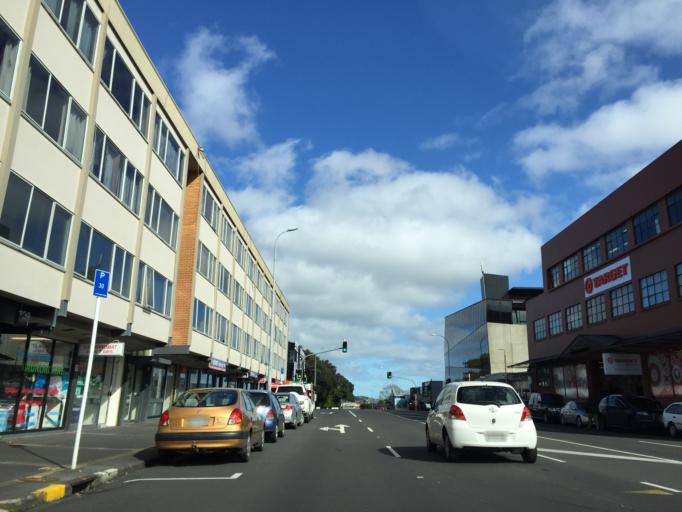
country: NZ
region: Auckland
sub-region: Auckland
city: Auckland
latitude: -36.8714
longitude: 174.7526
